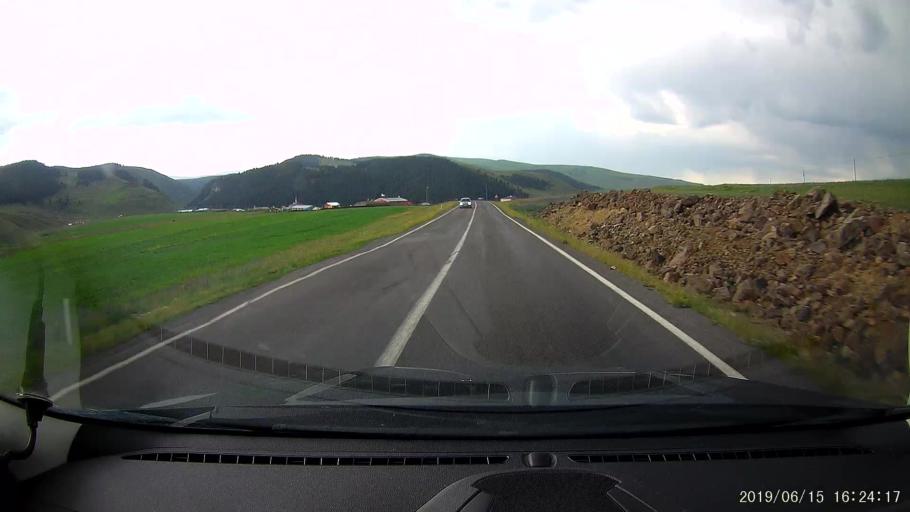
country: TR
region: Ardahan
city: Hanak
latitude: 41.1665
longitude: 42.8694
